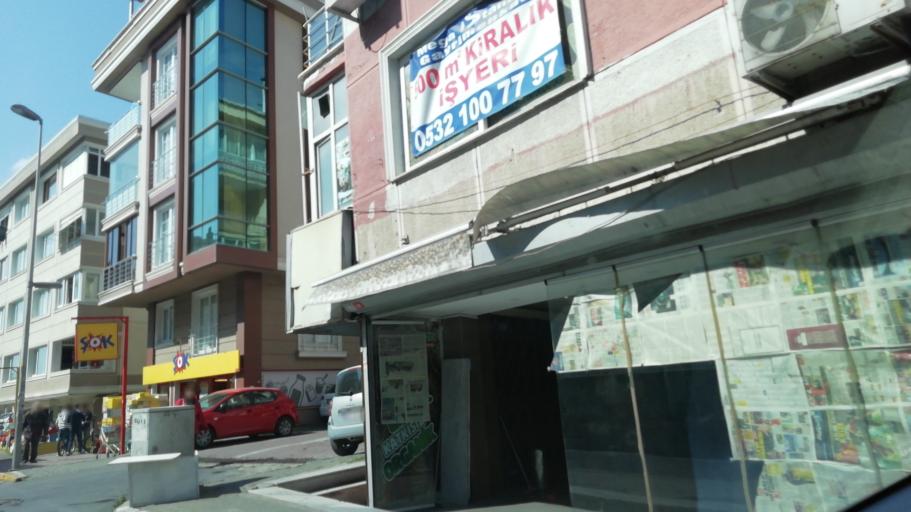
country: TR
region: Istanbul
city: Yakuplu
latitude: 40.9735
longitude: 28.7327
